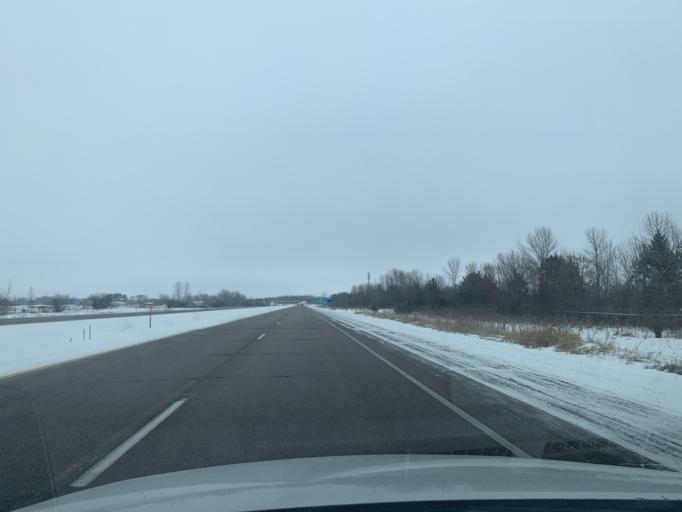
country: US
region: Minnesota
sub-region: Chisago County
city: Rush City
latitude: 45.6751
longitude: -92.9917
